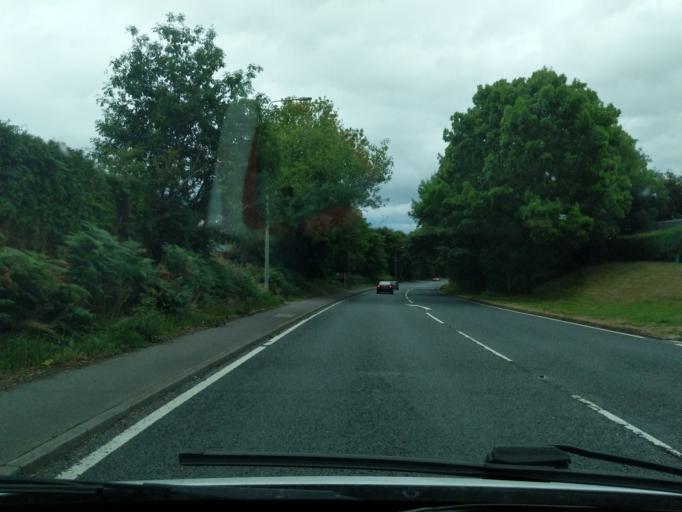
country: GB
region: England
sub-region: Cheshire West and Chester
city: Cuddington
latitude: 53.2448
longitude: -2.5990
